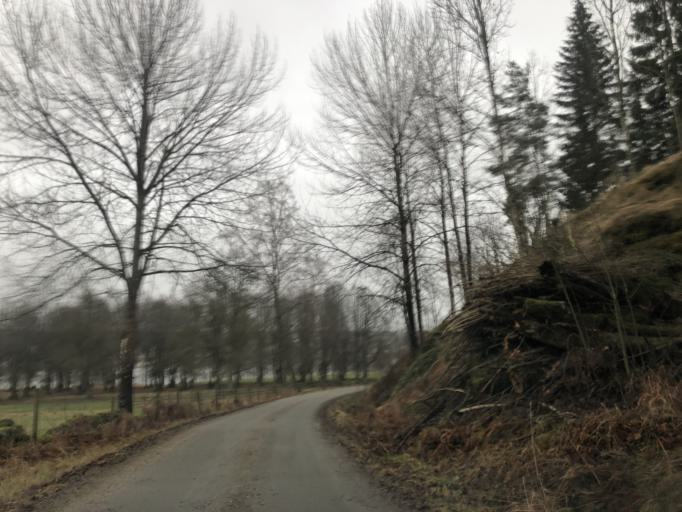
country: SE
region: Vaestra Goetaland
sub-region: Ulricehamns Kommun
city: Ulricehamn
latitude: 57.7949
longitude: 13.3890
